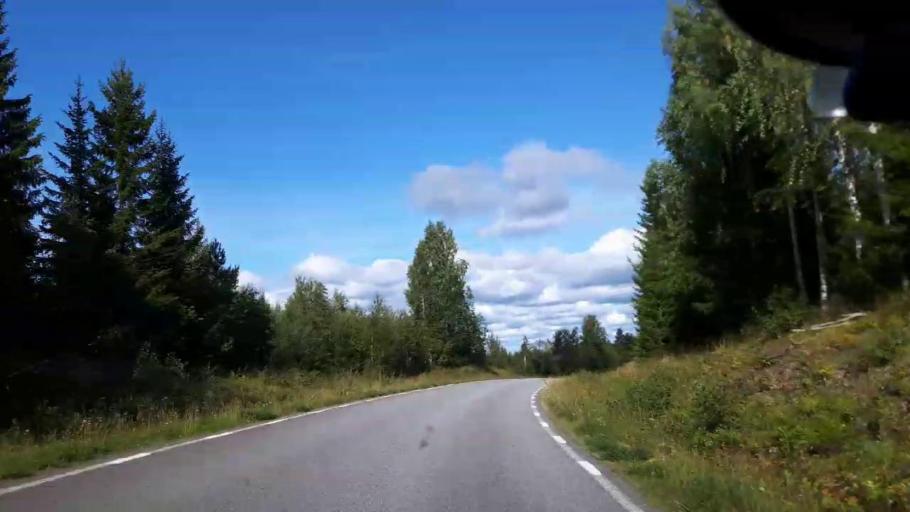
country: SE
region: Jaemtland
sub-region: OEstersunds Kommun
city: Brunflo
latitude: 63.2158
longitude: 15.2448
